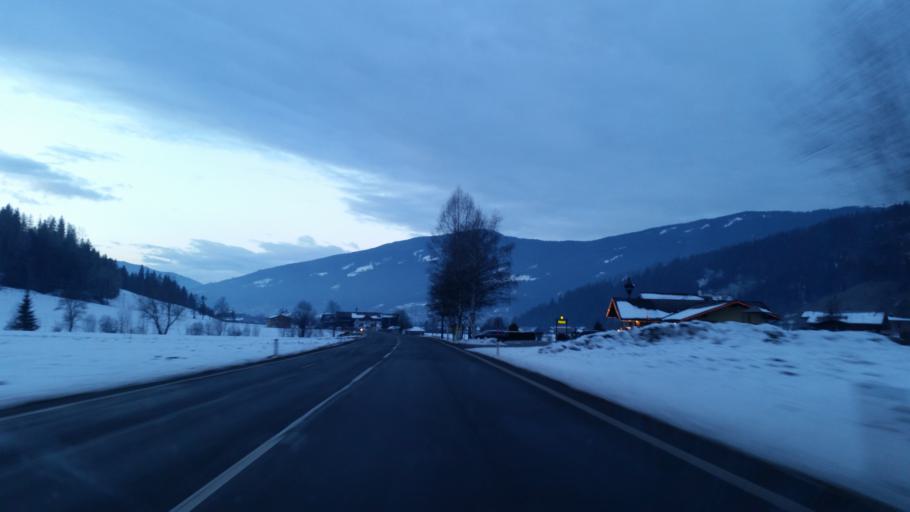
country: AT
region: Salzburg
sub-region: Politischer Bezirk Sankt Johann im Pongau
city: Forstau
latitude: 47.3625
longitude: 13.4928
